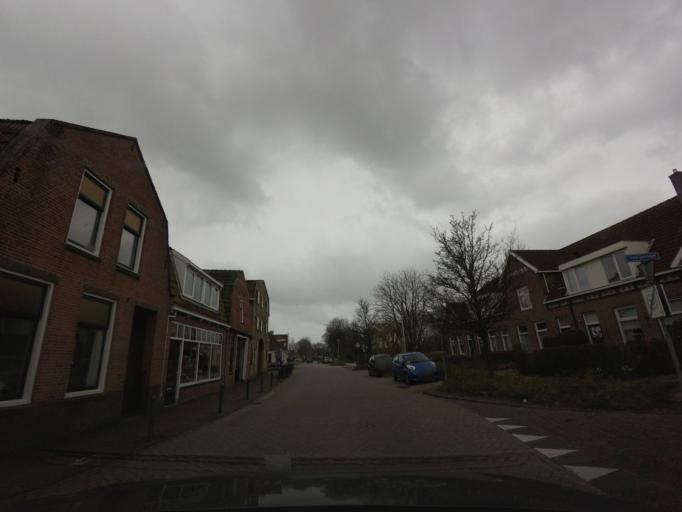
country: NL
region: Friesland
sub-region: Gemeente Franekeradeel
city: Franeker
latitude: 53.1852
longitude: 5.5377
